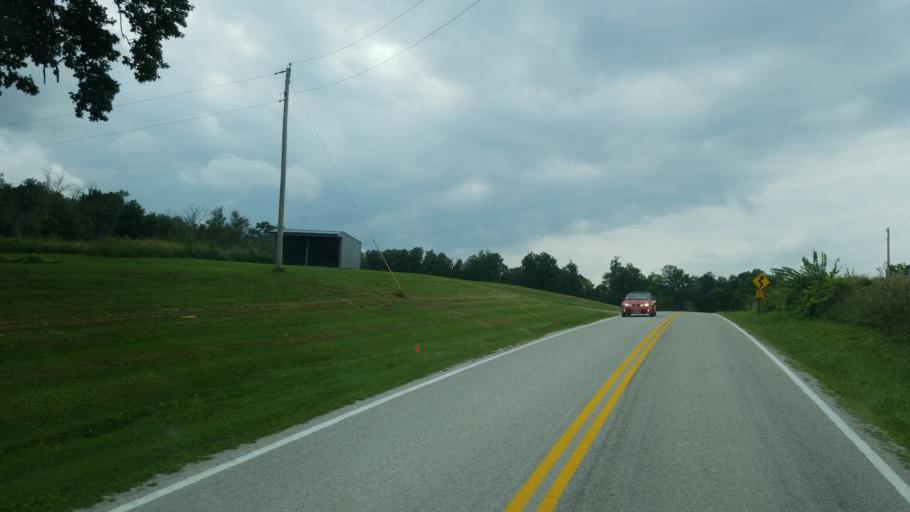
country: US
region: Ohio
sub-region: Ashland County
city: Loudonville
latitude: 40.6324
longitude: -82.3704
